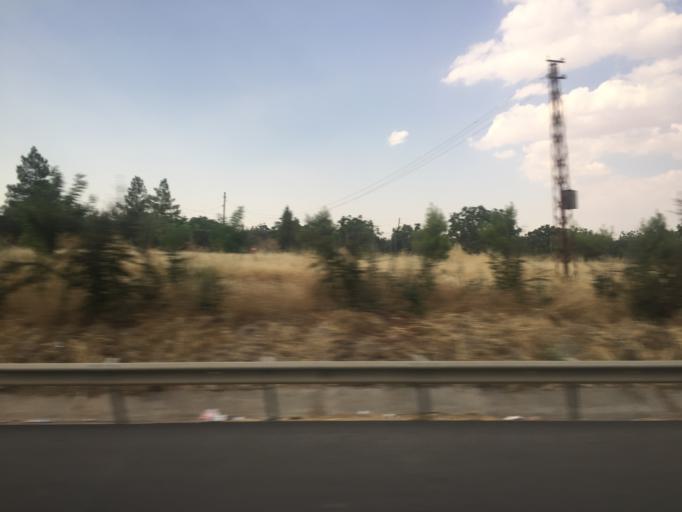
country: TR
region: Sanliurfa
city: Akziyaret
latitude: 37.2691
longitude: 38.7918
